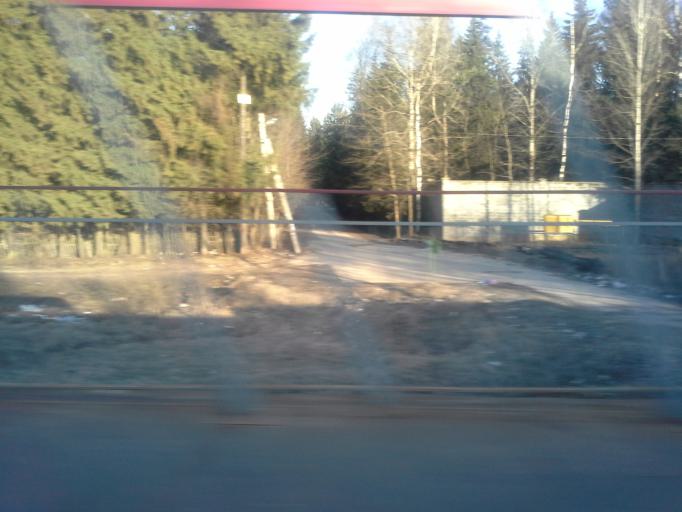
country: RU
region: Moskovskaya
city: Nekrasovskiy
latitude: 56.1209
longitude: 37.5151
